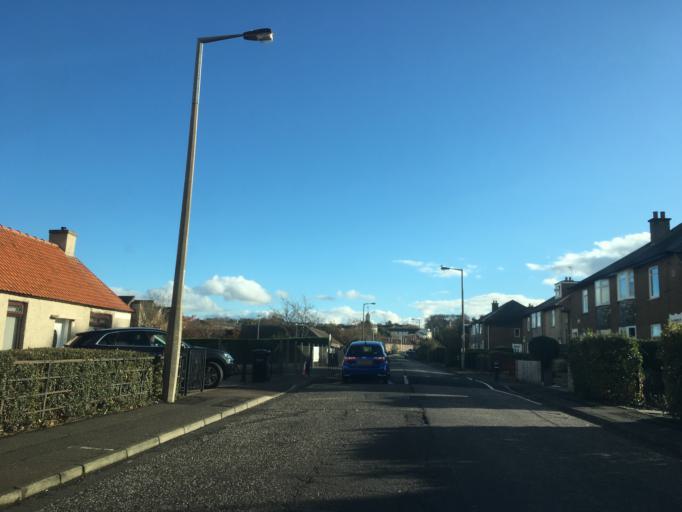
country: GB
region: Scotland
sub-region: Edinburgh
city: Colinton
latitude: 55.9108
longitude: -3.2308
